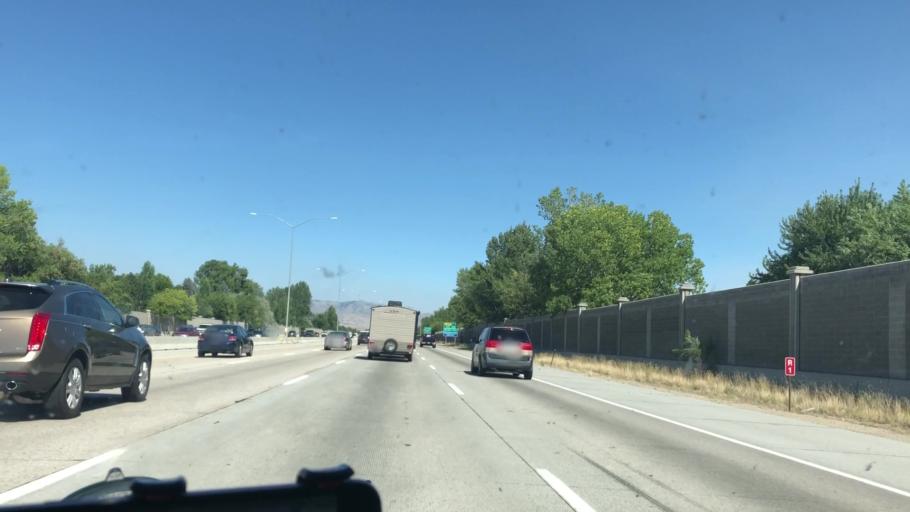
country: US
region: Idaho
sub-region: Ada County
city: Garden City
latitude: 43.5972
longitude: -116.3090
